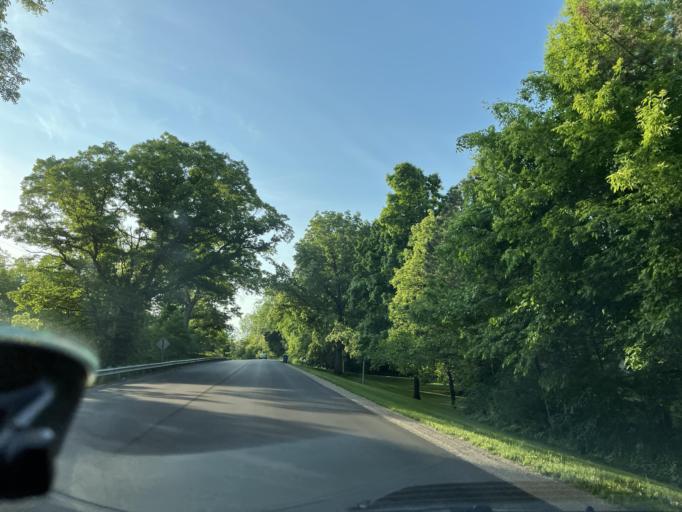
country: US
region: Michigan
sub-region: Barry County
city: Middleville
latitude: 42.7118
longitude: -85.4445
